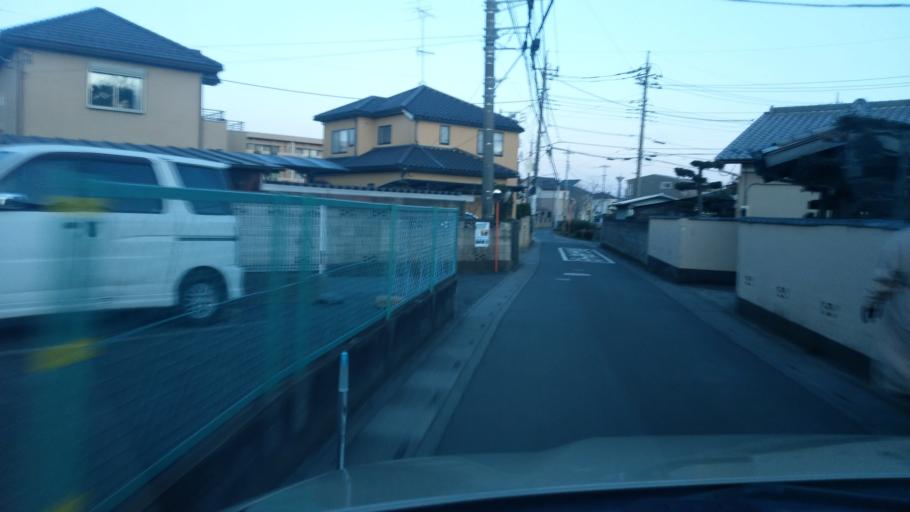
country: JP
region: Saitama
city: Ageoshimo
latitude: 35.9184
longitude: 139.5821
